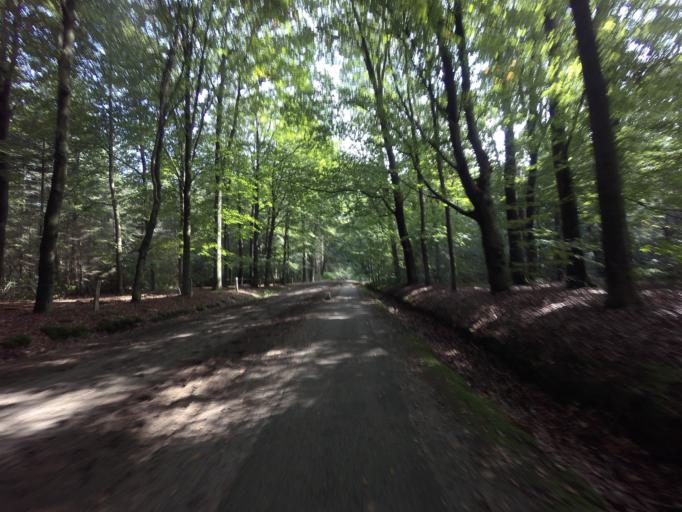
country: NL
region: Overijssel
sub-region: Gemeente Enschede
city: Enschede
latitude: 52.2575
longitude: 6.8546
